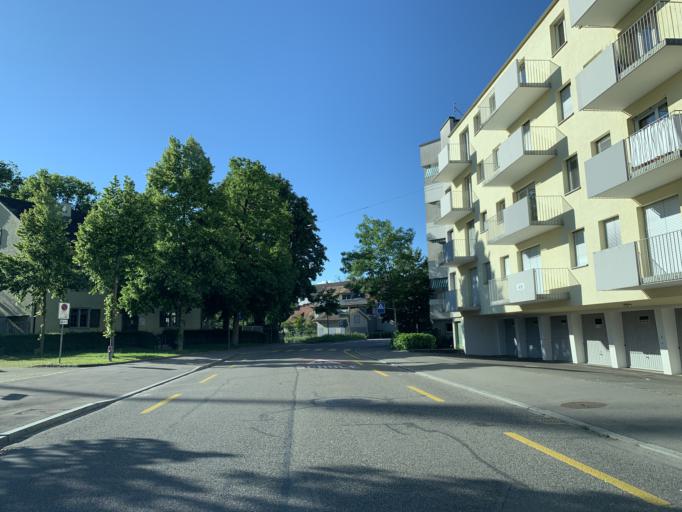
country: CH
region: Zurich
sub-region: Bezirk Winterthur
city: Stadt Winterthur (Kreis 1) / Neuwiesen
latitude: 47.5014
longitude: 8.7184
